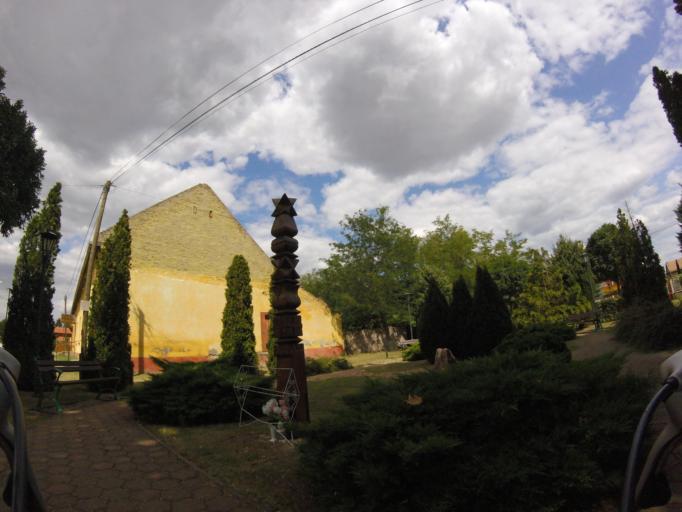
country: HU
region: Bacs-Kiskun
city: Tompa
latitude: 46.1279
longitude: 19.4716
